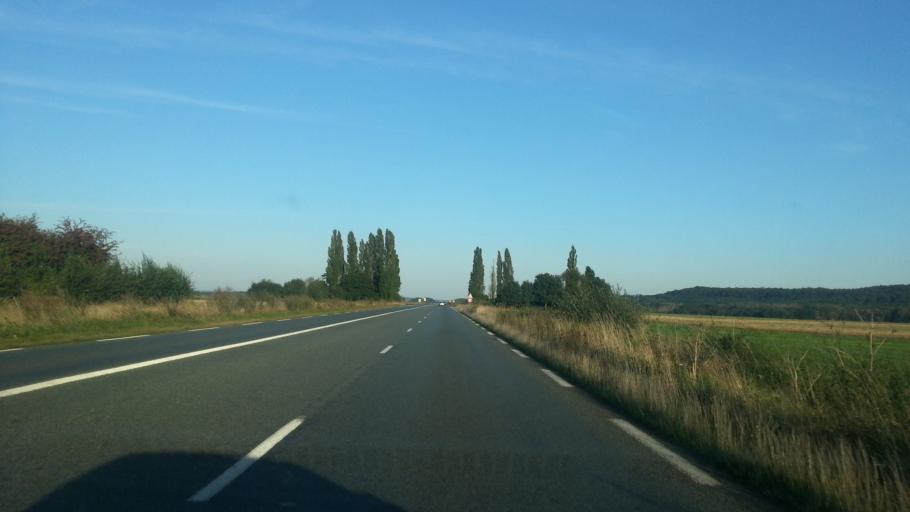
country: FR
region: Picardie
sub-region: Departement de l'Oise
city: Remy
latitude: 49.4029
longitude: 2.7191
